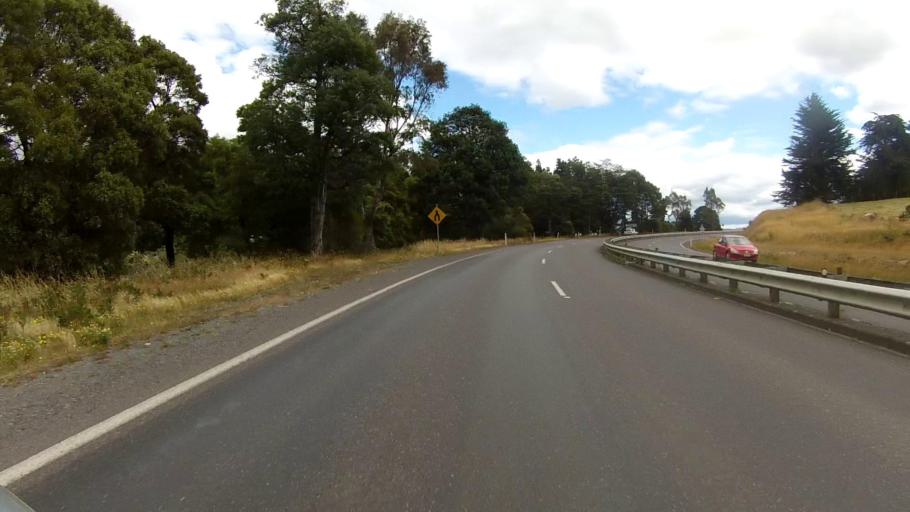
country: AU
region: Tasmania
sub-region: Kingborough
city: Margate
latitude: -42.9790
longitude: 147.1641
